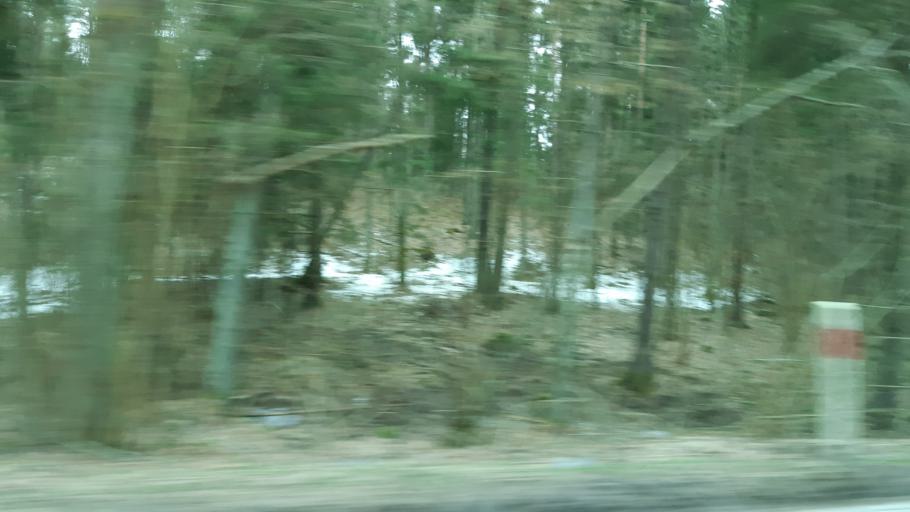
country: PL
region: Podlasie
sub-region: Suwalki
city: Suwalki
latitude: 54.2926
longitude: 22.9572
